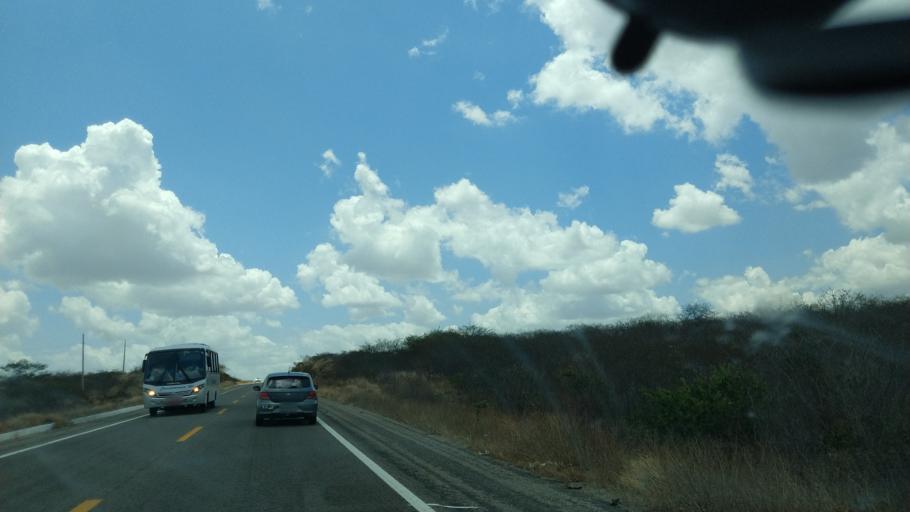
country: BR
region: Rio Grande do Norte
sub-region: Cerro Cora
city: Cerro Cora
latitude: -6.2011
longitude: -36.3359
